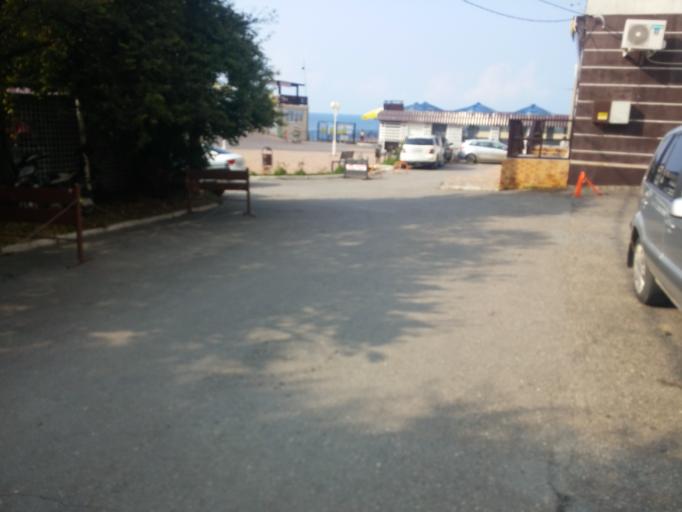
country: RU
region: Krasnodarskiy
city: Divnomorskoye
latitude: 44.4629
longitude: 38.1522
